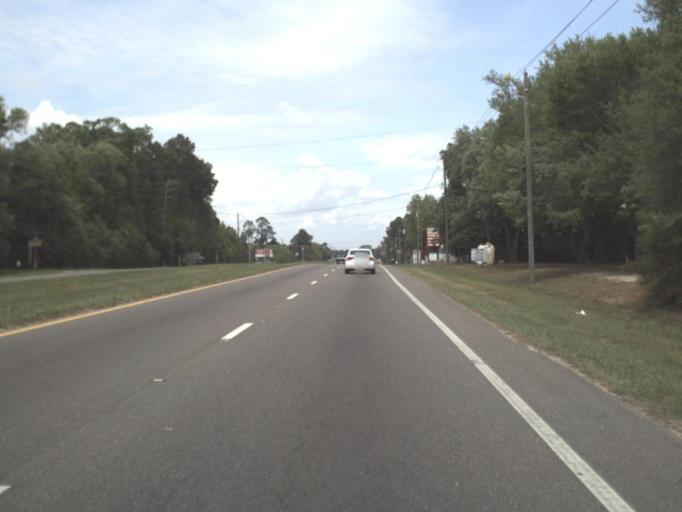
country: US
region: Florida
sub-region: Escambia County
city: Bellview
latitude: 30.4934
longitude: -87.3060
